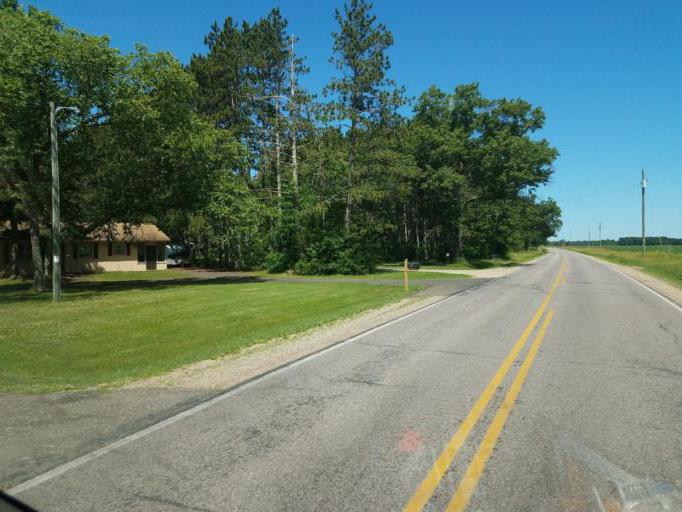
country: US
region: Wisconsin
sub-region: Adams County
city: Adams
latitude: 43.8479
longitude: -89.9257
